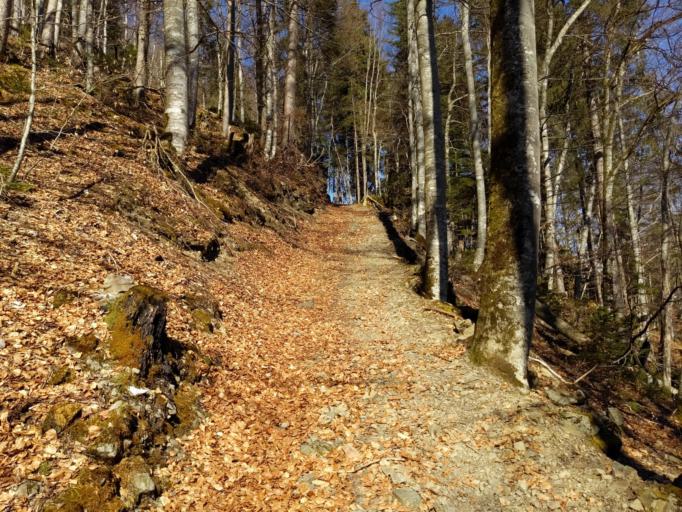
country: CH
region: Glarus
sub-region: Glarus
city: Luchsingen
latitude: 46.9475
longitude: 9.0181
